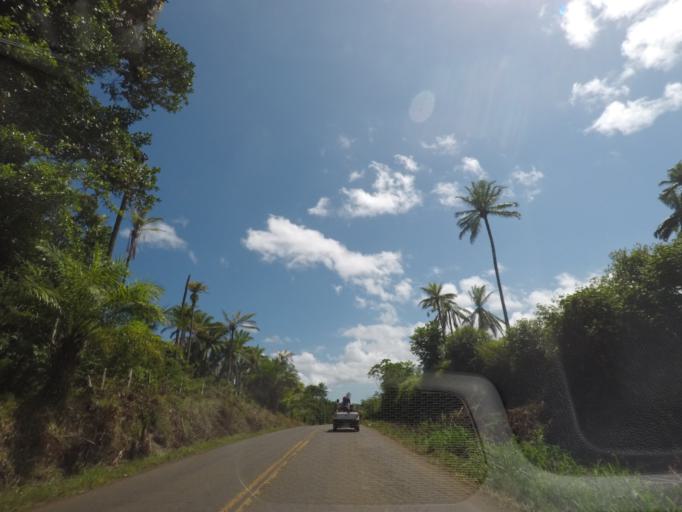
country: BR
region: Bahia
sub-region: Taperoa
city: Taperoa
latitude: -13.5044
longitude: -39.0937
